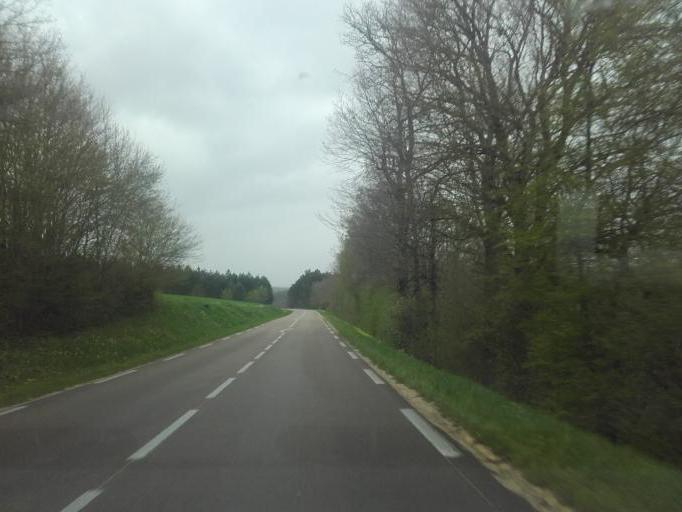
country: FR
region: Bourgogne
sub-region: Departement de l'Yonne
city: Chablis
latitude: 47.7351
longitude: 3.8455
